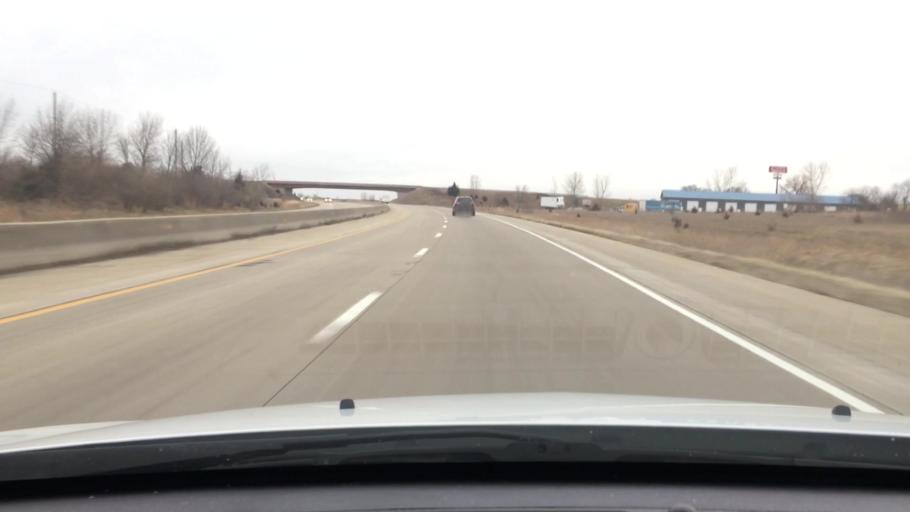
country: US
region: Illinois
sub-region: McLean County
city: Hudson
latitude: 40.6665
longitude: -89.0074
